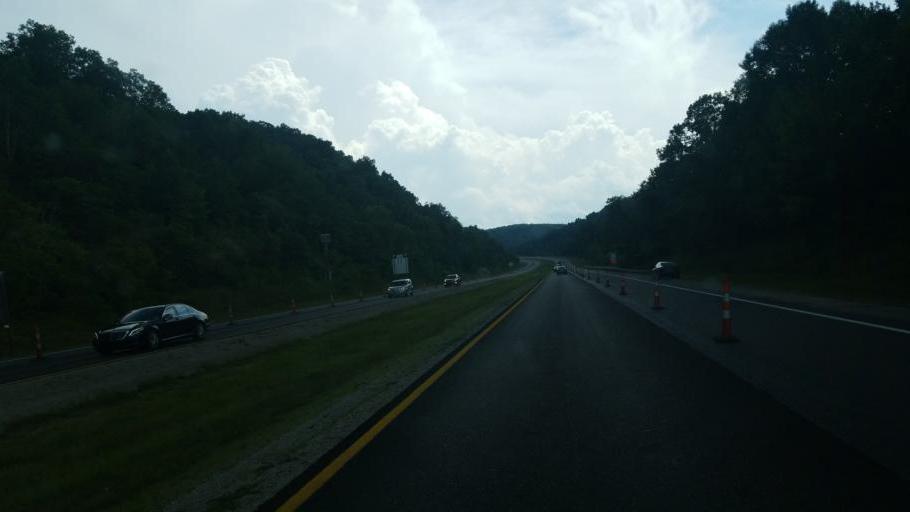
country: US
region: West Virginia
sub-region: Kanawha County
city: Alum Creek
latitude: 38.2616
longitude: -81.8339
